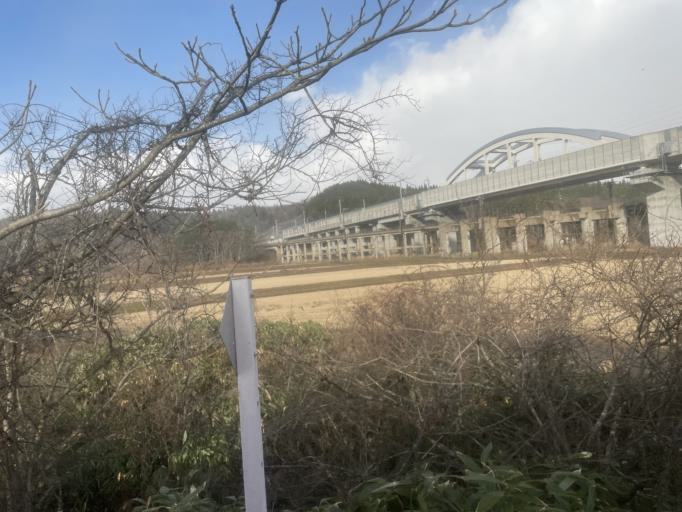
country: JP
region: Aomori
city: Goshogawara
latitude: 41.0658
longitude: 140.5616
